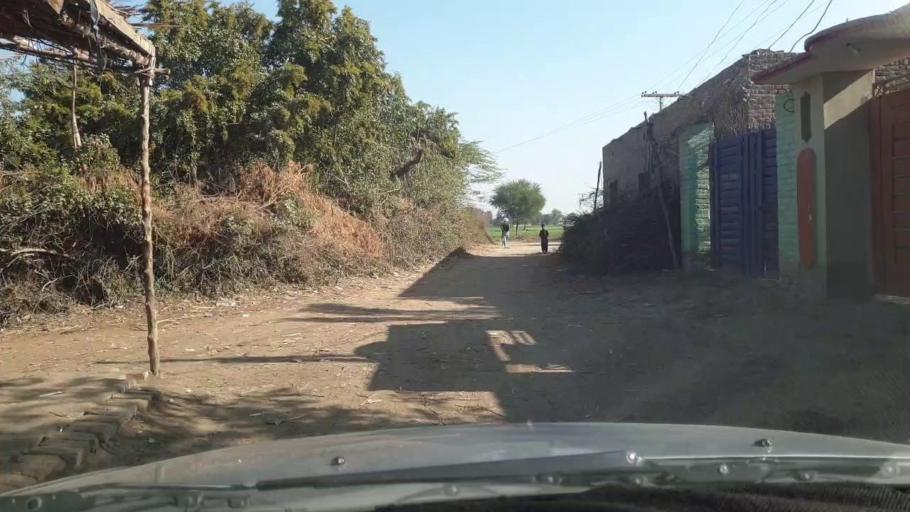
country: PK
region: Sindh
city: Mirpur Mathelo
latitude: 27.9753
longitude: 69.5507
